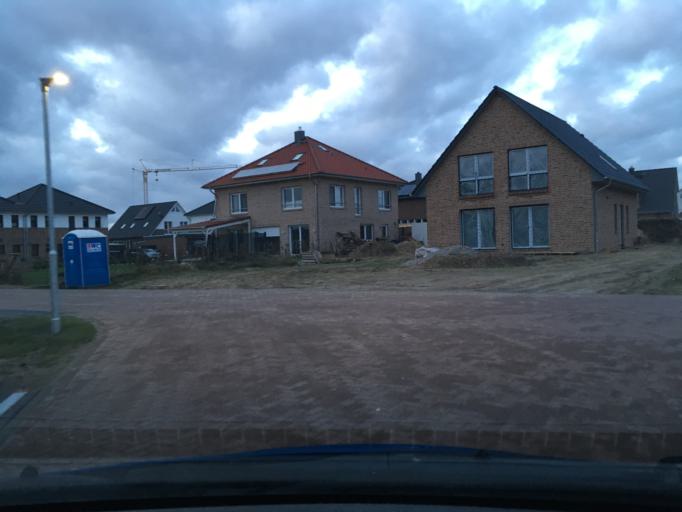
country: DE
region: Lower Saxony
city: Salzhausen
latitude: 53.2224
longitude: 10.1620
